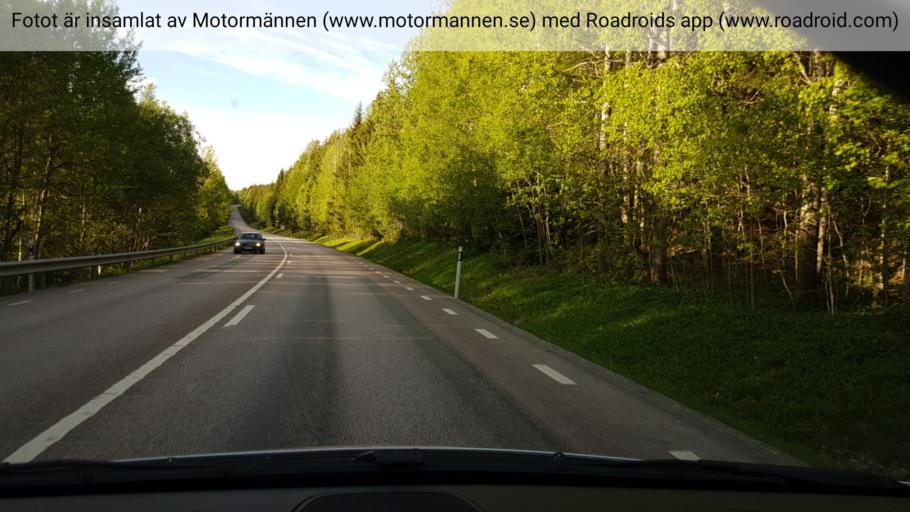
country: SE
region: Vaestmanland
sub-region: Fagersta Kommun
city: Fagersta
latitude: 59.9306
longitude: 15.7279
